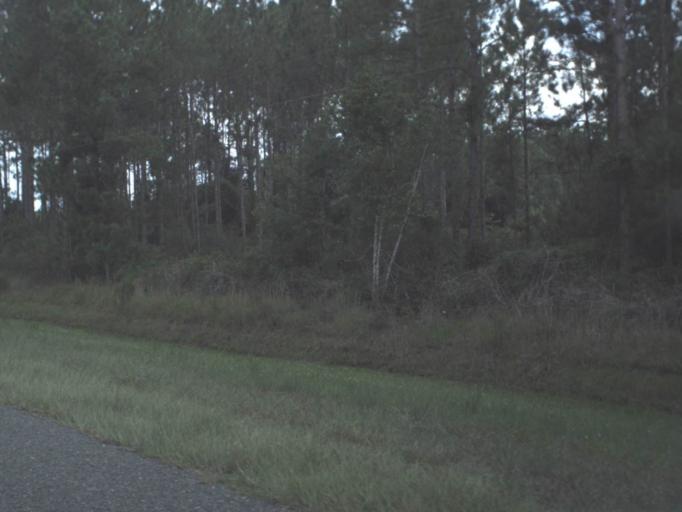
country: US
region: Florida
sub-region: Levy County
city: Chiefland
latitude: 29.3445
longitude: -82.7791
